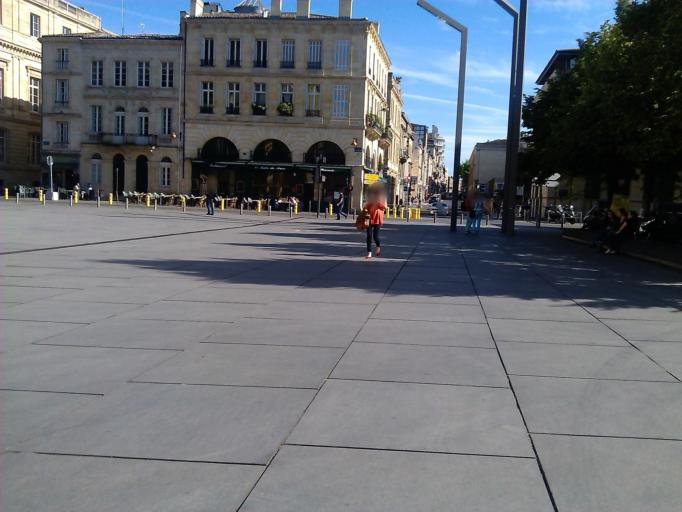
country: FR
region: Aquitaine
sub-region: Departement de la Gironde
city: Bordeaux
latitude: 44.8374
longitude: -0.5788
